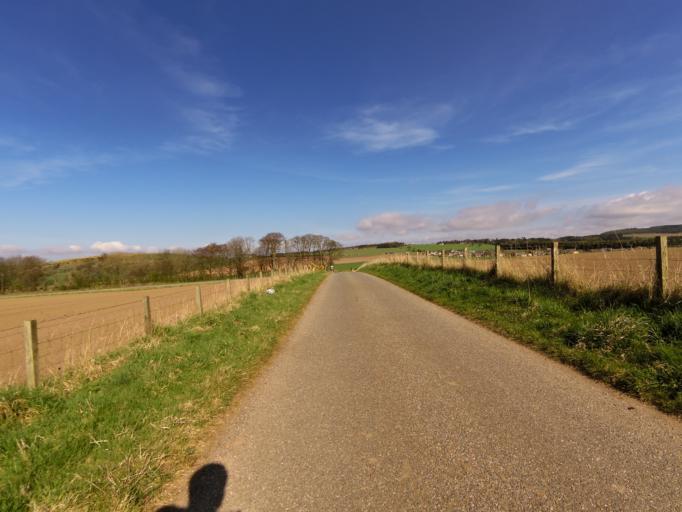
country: GB
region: Scotland
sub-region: Angus
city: Montrose
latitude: 56.7686
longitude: -2.4298
